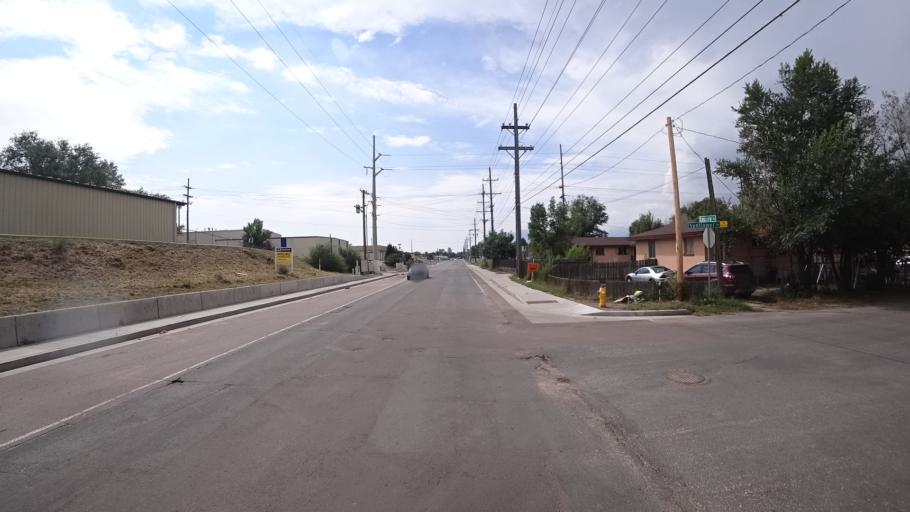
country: US
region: Colorado
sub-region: El Paso County
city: Colorado Springs
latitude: 38.8820
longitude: -104.8227
